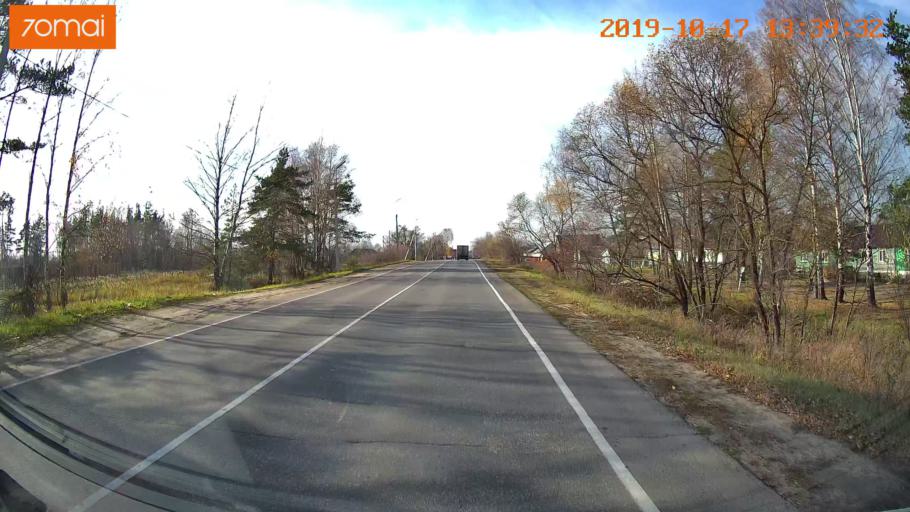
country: RU
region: Rjazan
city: Tuma
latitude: 55.1461
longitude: 40.5861
